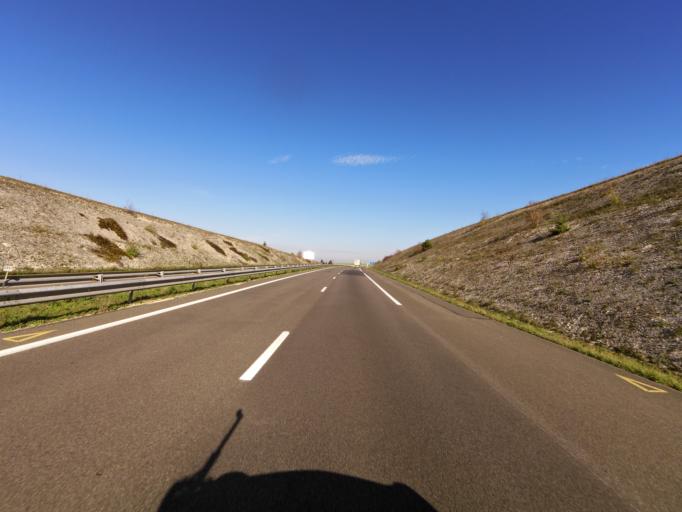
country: FR
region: Champagne-Ardenne
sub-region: Departement de la Marne
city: Fagnieres
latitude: 49.0390
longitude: 4.2813
